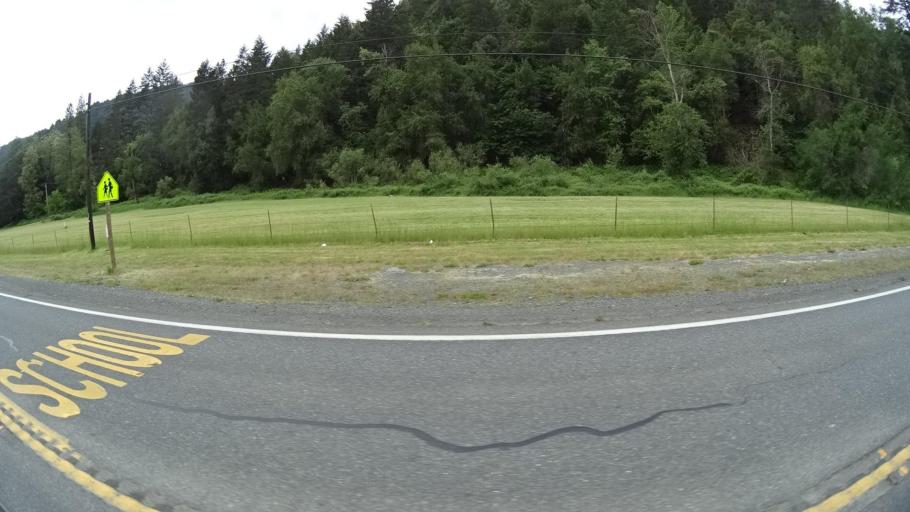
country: US
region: California
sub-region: Humboldt County
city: Willow Creek
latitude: 40.9517
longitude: -123.6402
